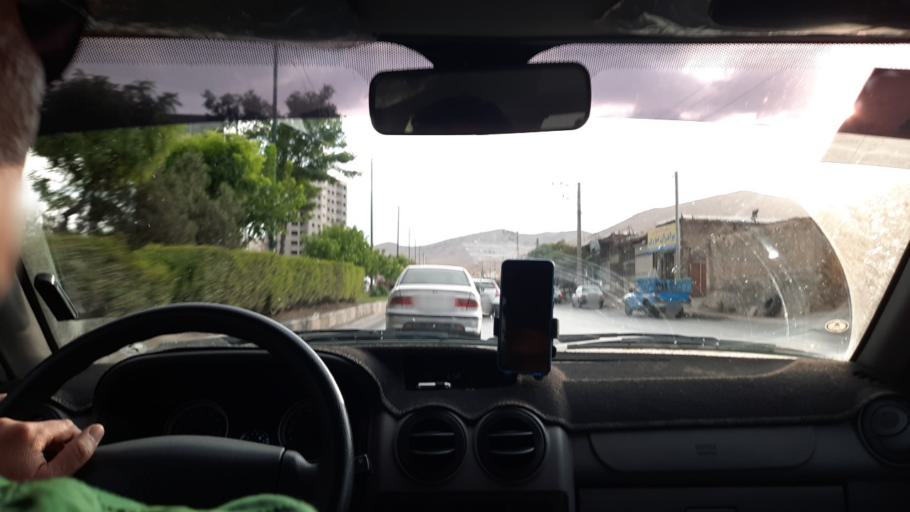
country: IR
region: Markazi
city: Arak
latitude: 34.0743
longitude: 49.6348
